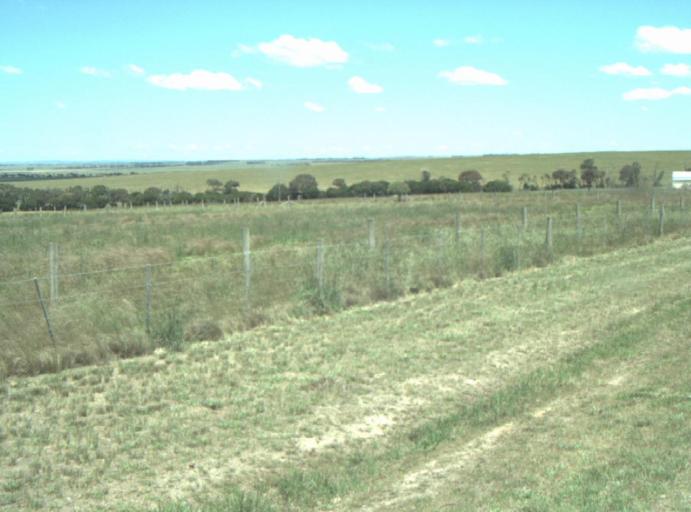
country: AU
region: Victoria
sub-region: Greater Geelong
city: Lara
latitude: -37.8925
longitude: 144.3709
